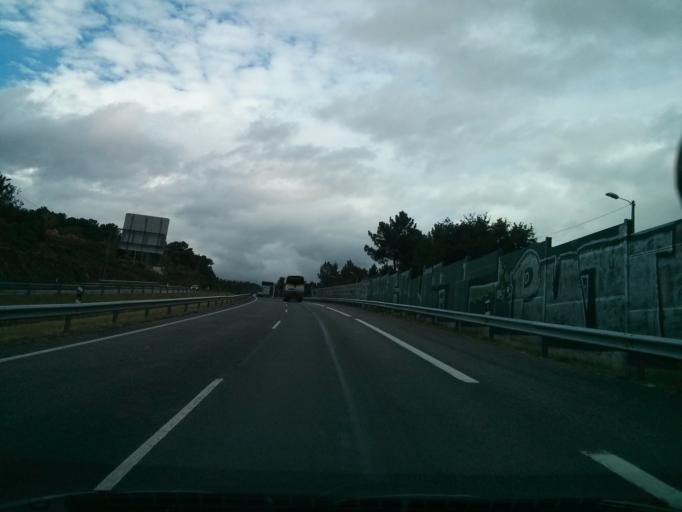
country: ES
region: Galicia
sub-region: Provincia de Ourense
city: Ourense
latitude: 42.3177
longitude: -7.8863
